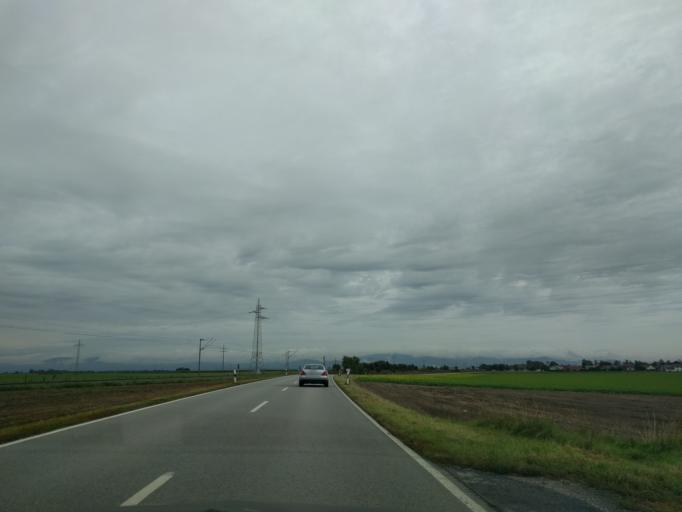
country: DE
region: Bavaria
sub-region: Lower Bavaria
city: Otzing
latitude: 48.7560
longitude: 12.7879
